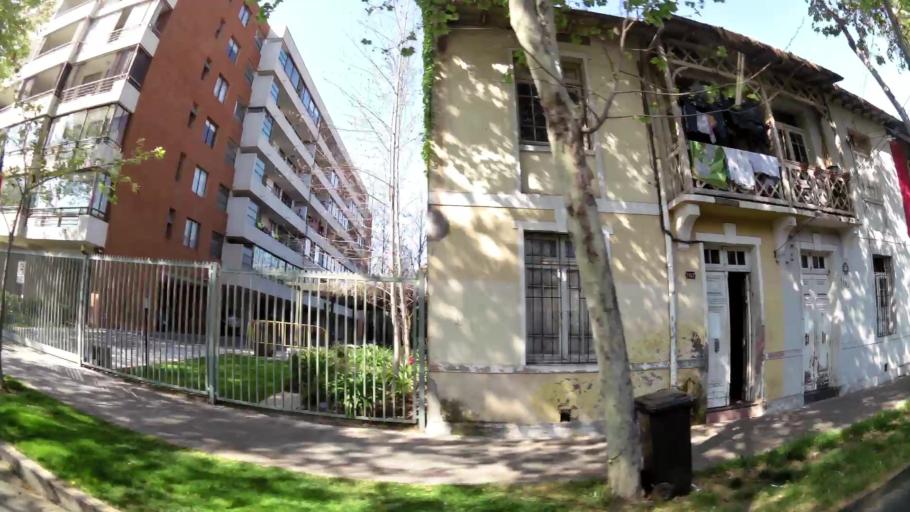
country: CL
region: Santiago Metropolitan
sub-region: Provincia de Santiago
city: Santiago
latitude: -33.4438
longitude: -70.6217
